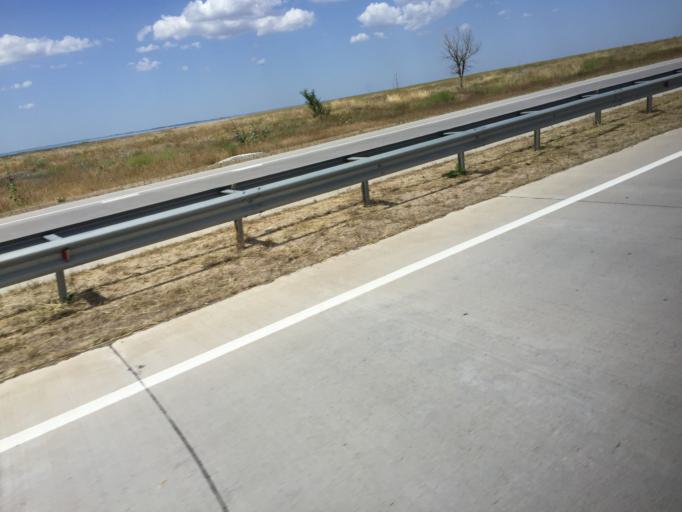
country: KZ
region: Ongtustik Qazaqstan
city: Temirlanovka
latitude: 42.7140
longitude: 69.2079
